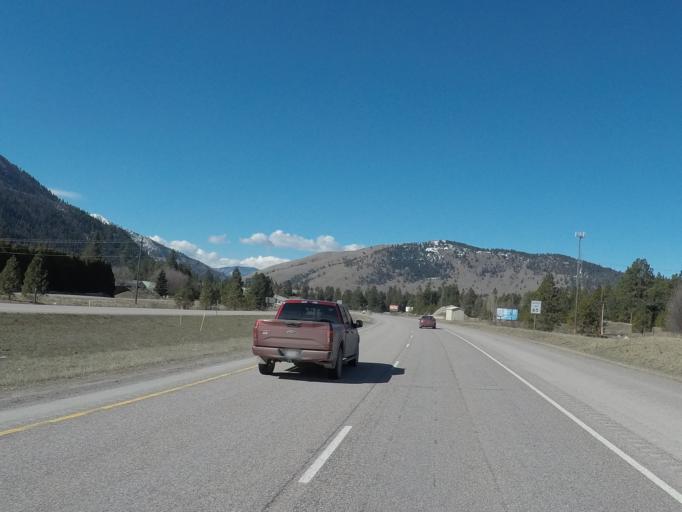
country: US
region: Montana
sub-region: Missoula County
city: Bonner-West Riverside
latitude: 46.8794
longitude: -113.9031
